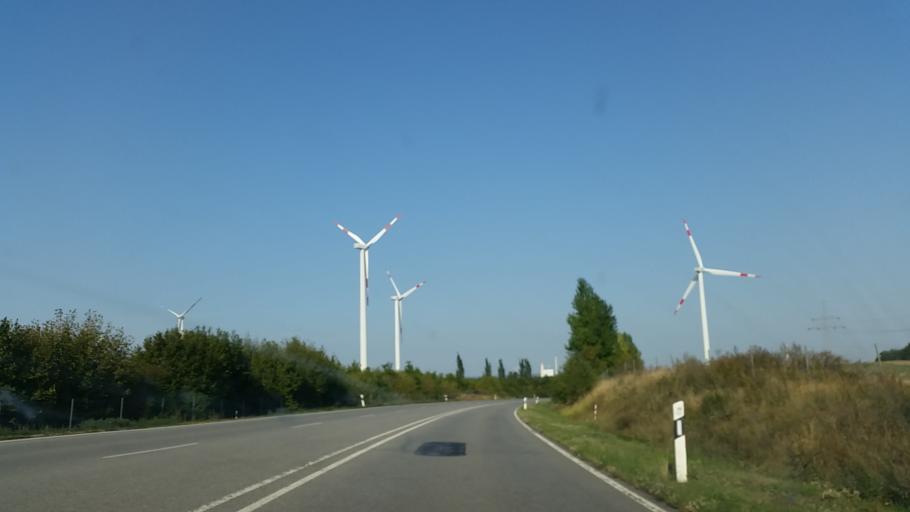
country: DE
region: Brandenburg
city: Meyenburg
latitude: 53.0831
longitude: 14.1764
